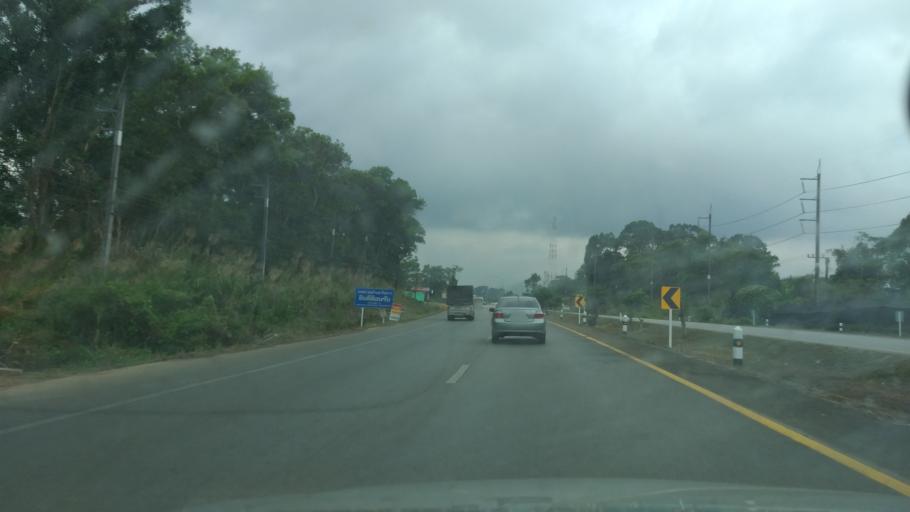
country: TH
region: Chanthaburi
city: Khlung
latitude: 12.4534
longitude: 102.2815
